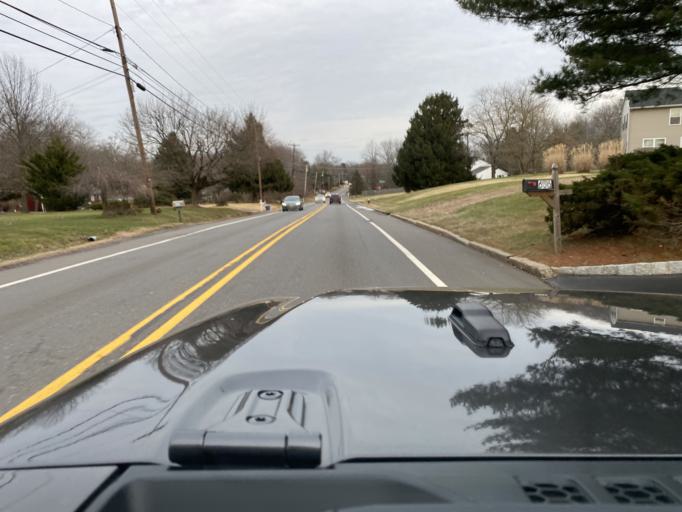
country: US
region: New Jersey
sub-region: Somerset County
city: Bloomingdale
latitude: 40.5018
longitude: -74.7000
